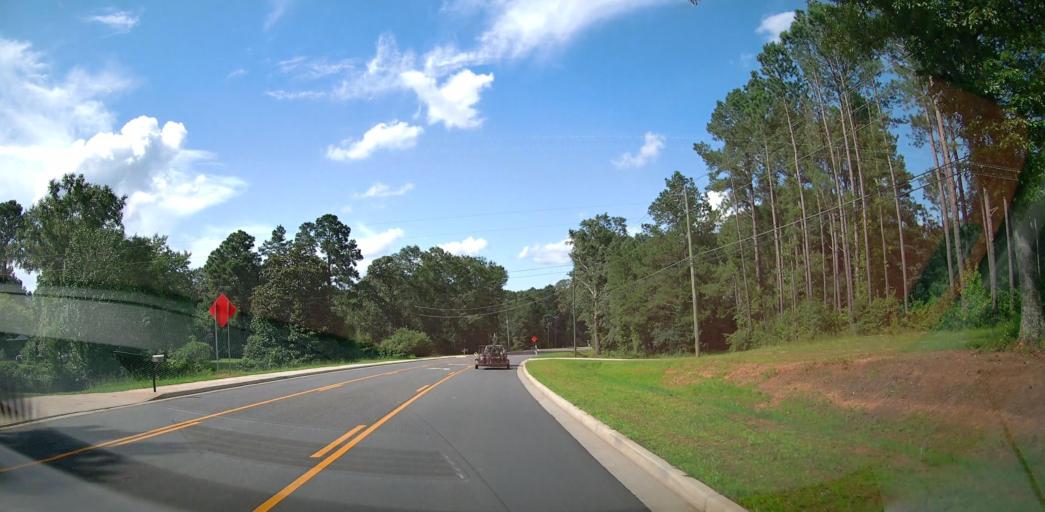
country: US
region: Georgia
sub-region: Houston County
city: Perry
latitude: 32.5008
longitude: -83.6995
